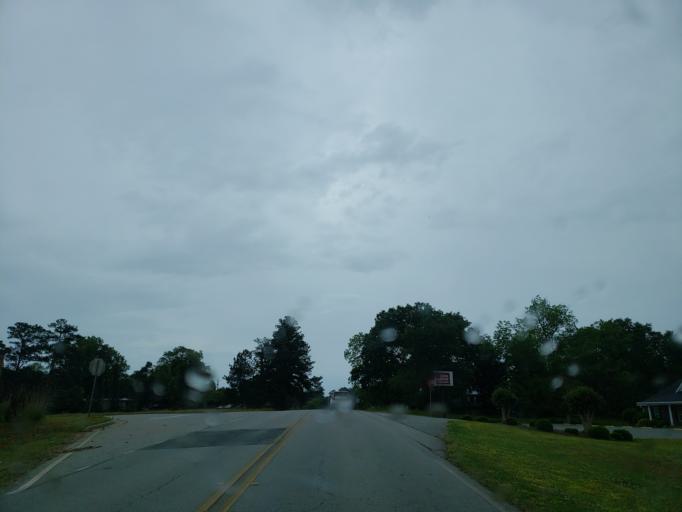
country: US
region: Georgia
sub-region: Haralson County
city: Buchanan
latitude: 33.8144
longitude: -85.1926
